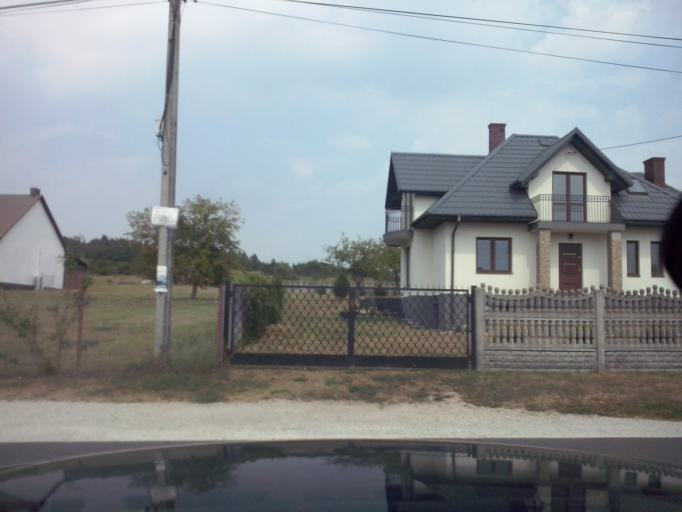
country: PL
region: Swietokrzyskie
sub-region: Powiat kielecki
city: Brzeziny
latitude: 50.7554
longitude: 20.5601
